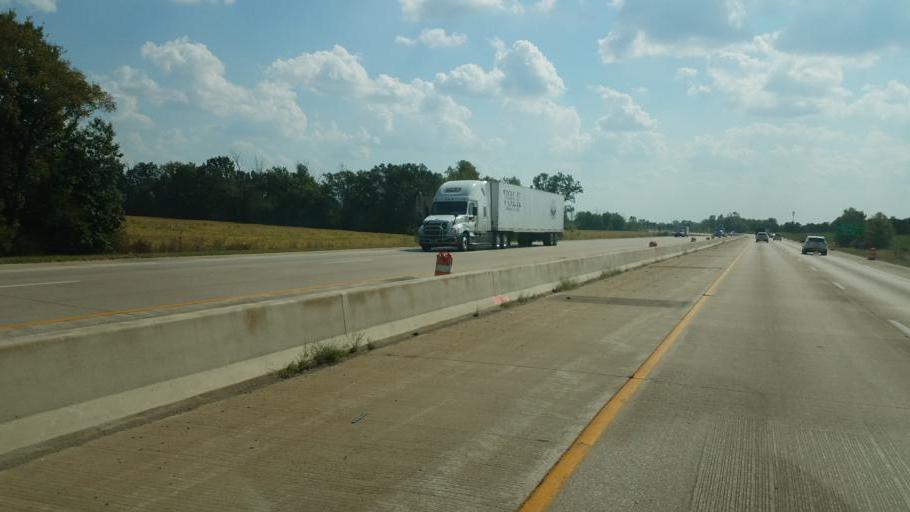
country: US
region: Indiana
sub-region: Allen County
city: Leo-Cedarville
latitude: 41.1441
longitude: -85.0150
